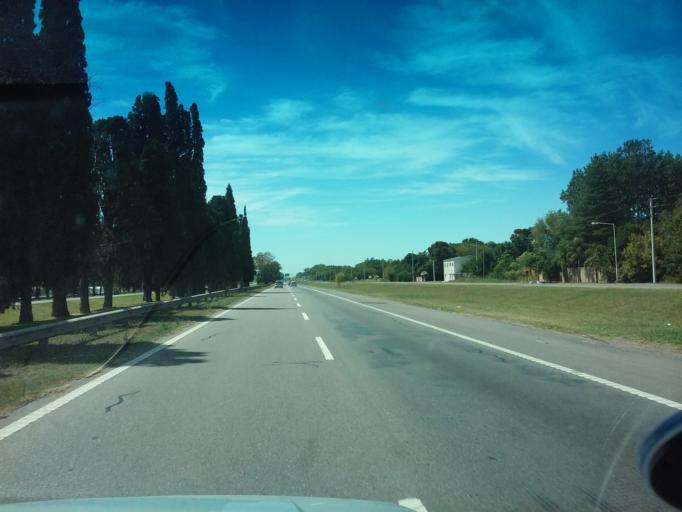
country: AR
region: Buenos Aires
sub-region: Partido de Mercedes
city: Mercedes
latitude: -34.6600
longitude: -59.3739
